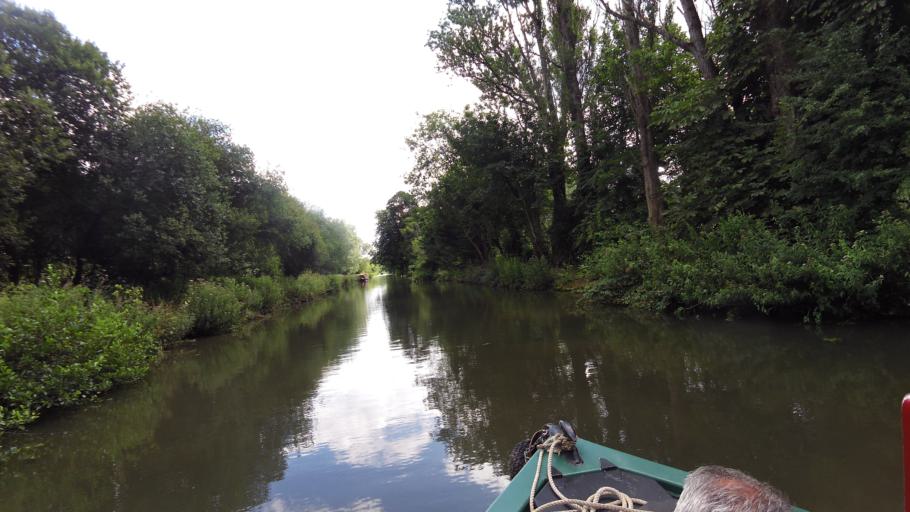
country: GB
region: England
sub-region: West Berkshire
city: Kintbury
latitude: 51.4004
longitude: -1.3901
